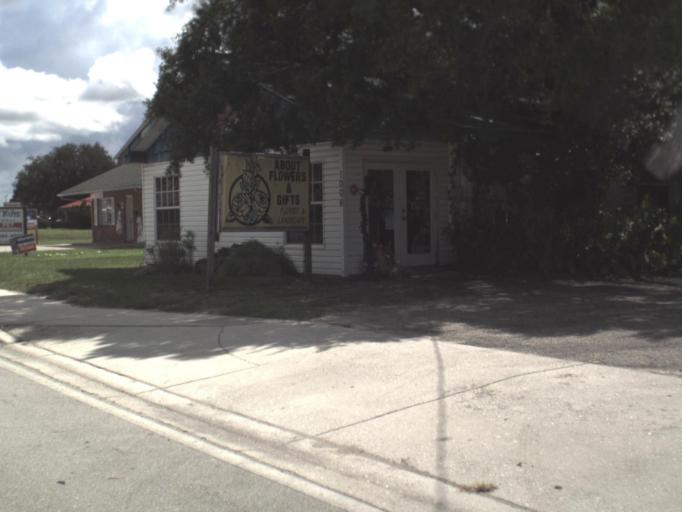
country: US
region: Florida
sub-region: DeSoto County
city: Arcadia
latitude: 27.2116
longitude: -81.8504
